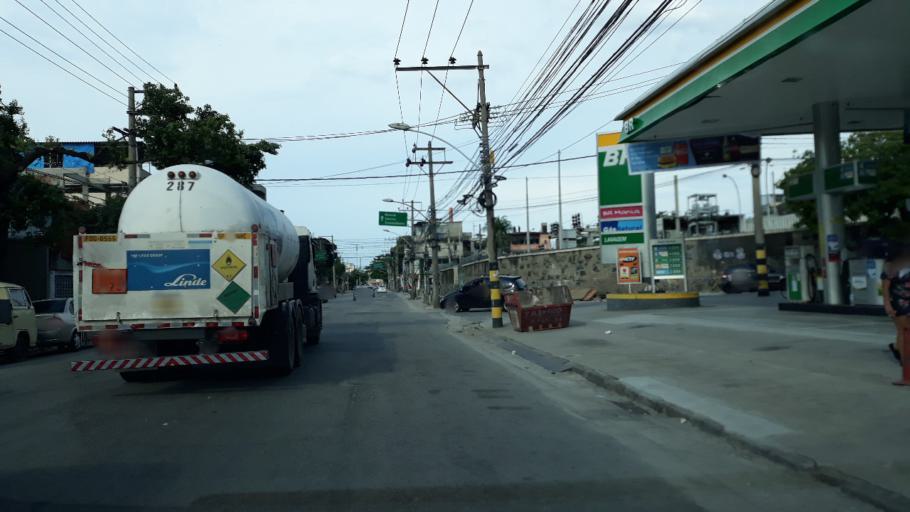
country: BR
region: Rio de Janeiro
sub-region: Rio De Janeiro
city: Rio de Janeiro
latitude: -22.8895
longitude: -43.2332
